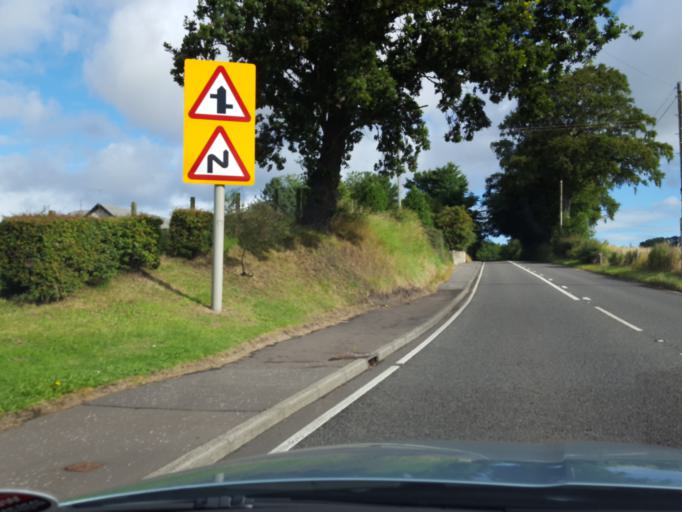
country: GB
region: Scotland
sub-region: West Lothian
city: Linlithgow
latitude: 55.9817
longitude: -3.6136
